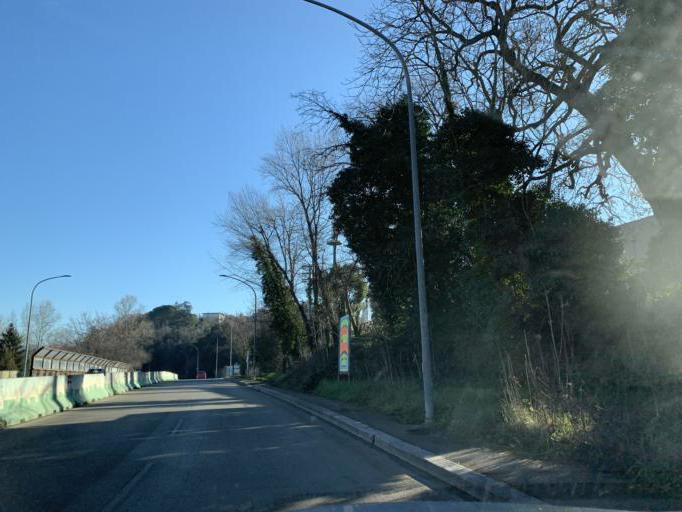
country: IT
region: Umbria
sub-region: Provincia di Terni
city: Terni
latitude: 42.5549
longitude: 12.6505
